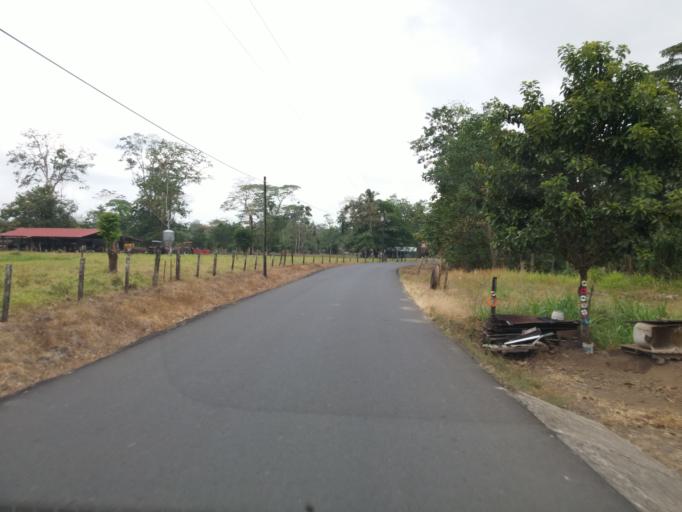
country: CR
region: Alajuela
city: Quesada
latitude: 10.3487
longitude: -84.5161
